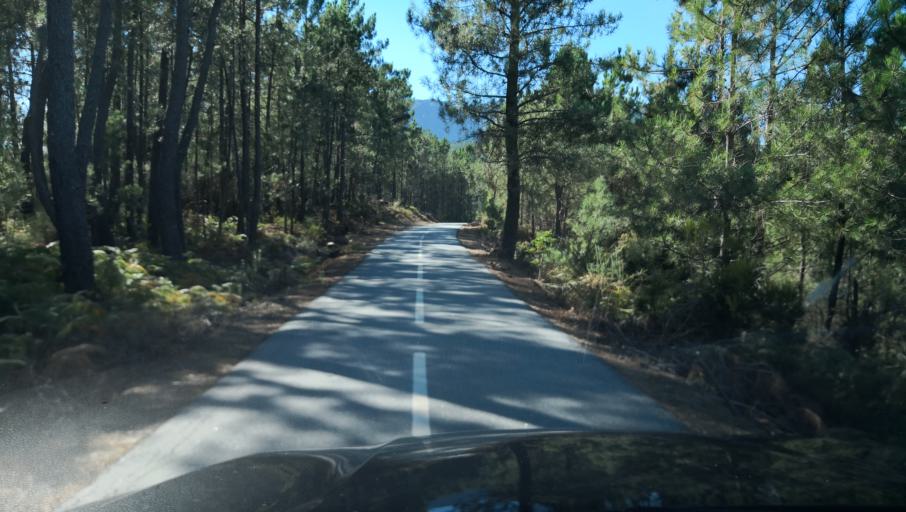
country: PT
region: Vila Real
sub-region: Santa Marta de Penaguiao
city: Santa Marta de Penaguiao
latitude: 41.2496
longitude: -7.8334
